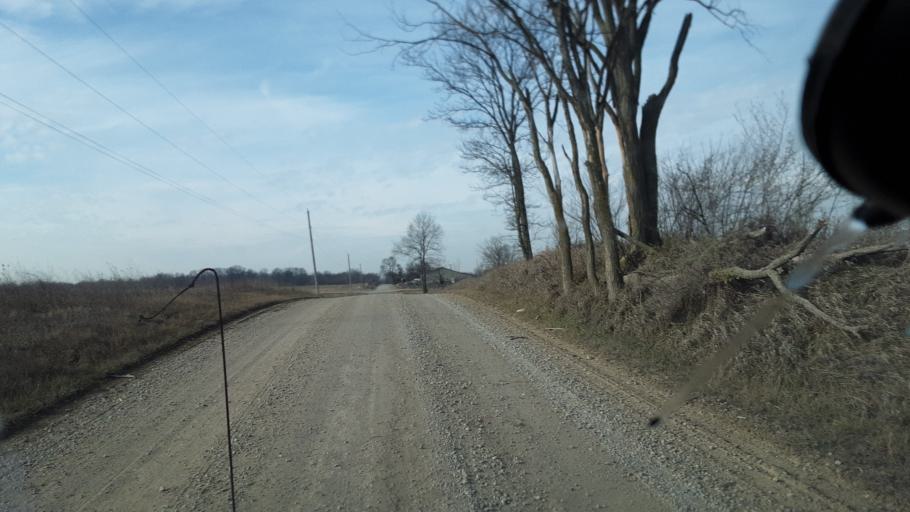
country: US
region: Indiana
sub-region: Allen County
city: Harlan
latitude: 41.2697
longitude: -84.8640
